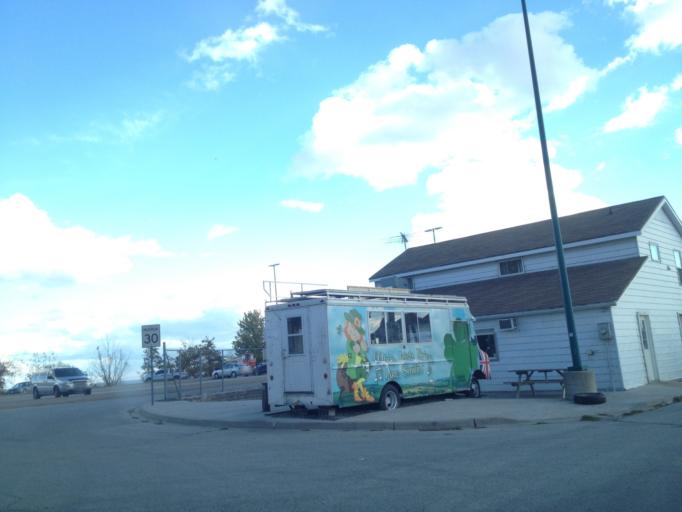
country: CA
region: Ontario
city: Amherstburg
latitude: 42.0280
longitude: -82.7326
